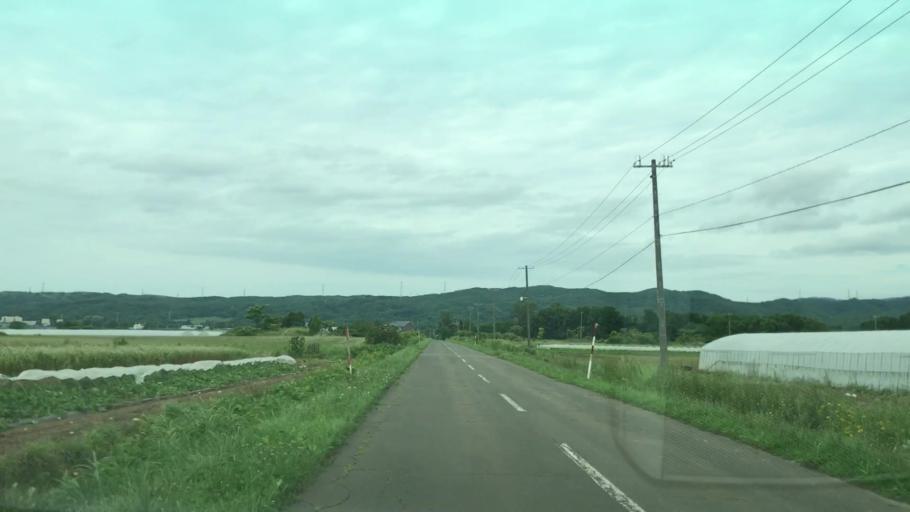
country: JP
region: Hokkaido
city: Iwanai
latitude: 43.0311
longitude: 140.5706
